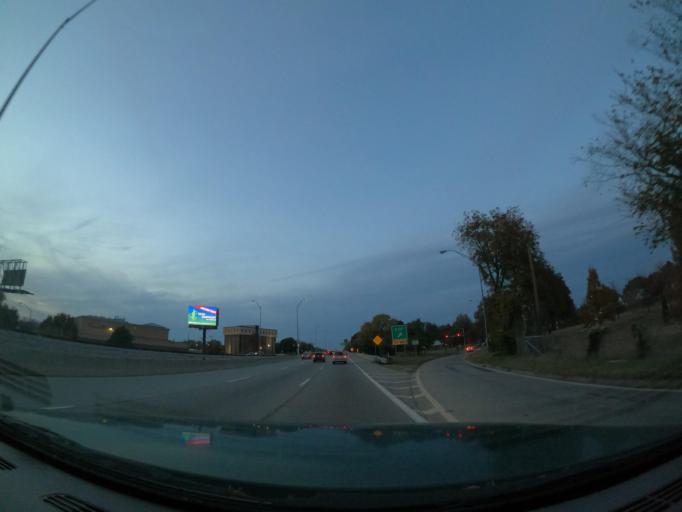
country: US
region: Oklahoma
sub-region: Tulsa County
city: Tulsa
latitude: 36.1323
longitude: -95.9480
